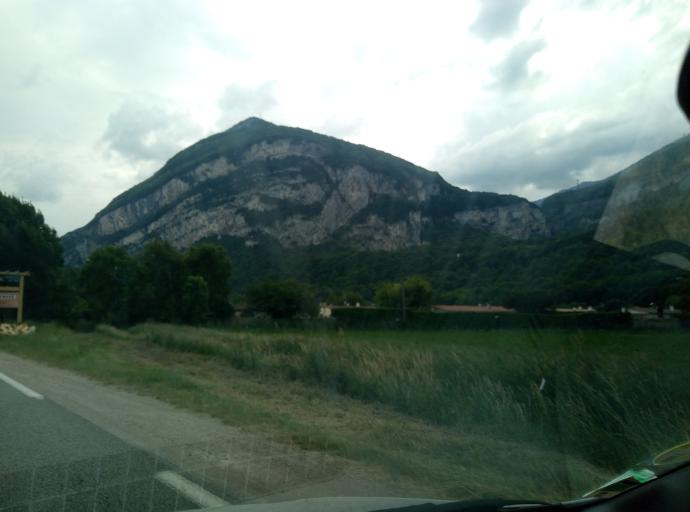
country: FR
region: Rhone-Alpes
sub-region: Departement de l'Isere
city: Sassenage
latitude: 45.2173
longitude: 5.6607
